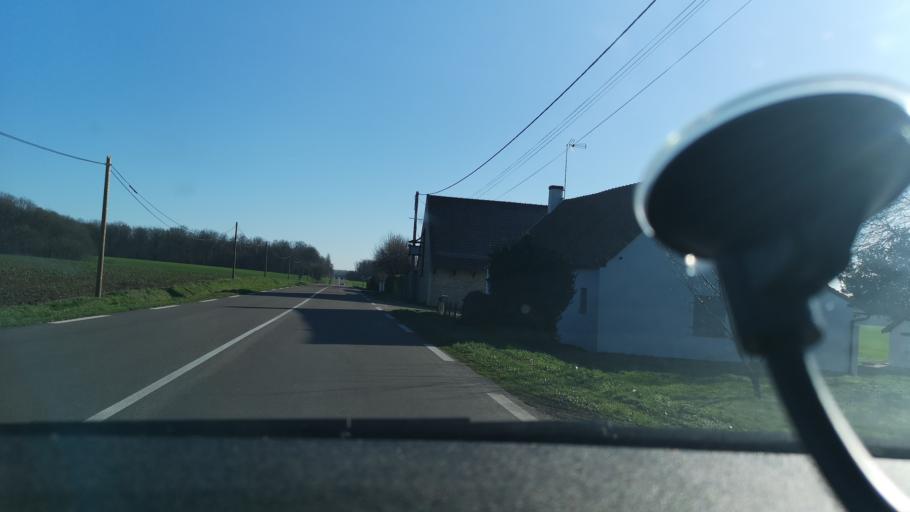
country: FR
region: Bourgogne
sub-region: Departement de Saone-et-Loire
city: Ouroux-sur-Saone
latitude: 46.7695
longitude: 4.9786
